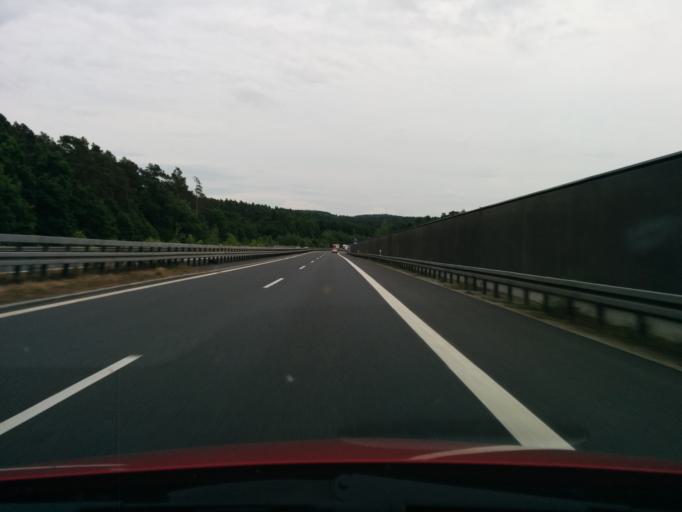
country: DE
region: Bavaria
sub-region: Upper Franconia
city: Zapfendorf
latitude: 50.0249
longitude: 10.9499
